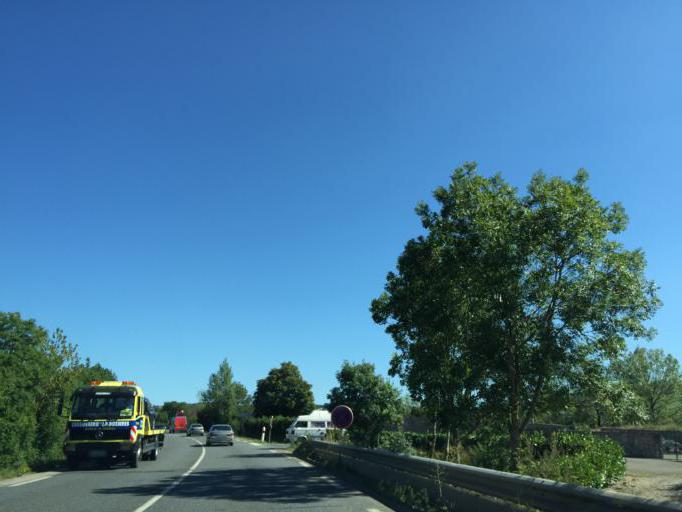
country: FR
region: Midi-Pyrenees
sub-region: Departement de l'Aveyron
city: Severac-le-Chateau
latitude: 44.3347
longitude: 3.0295
